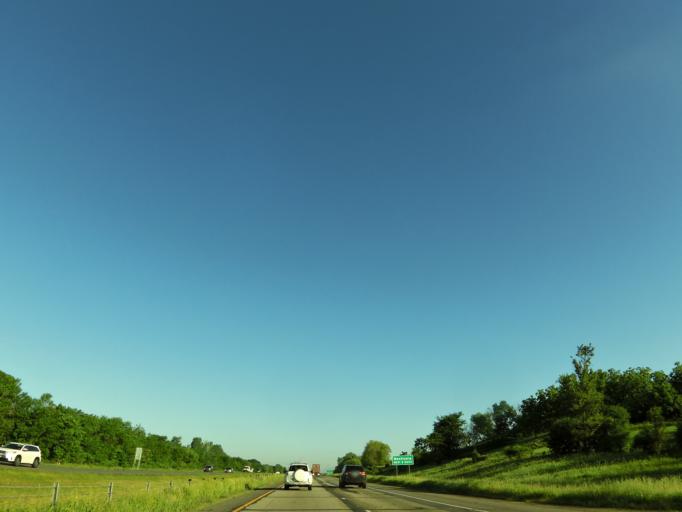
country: US
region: Minnesota
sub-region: Sherburne County
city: Big Lake
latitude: 45.2773
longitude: -93.7391
